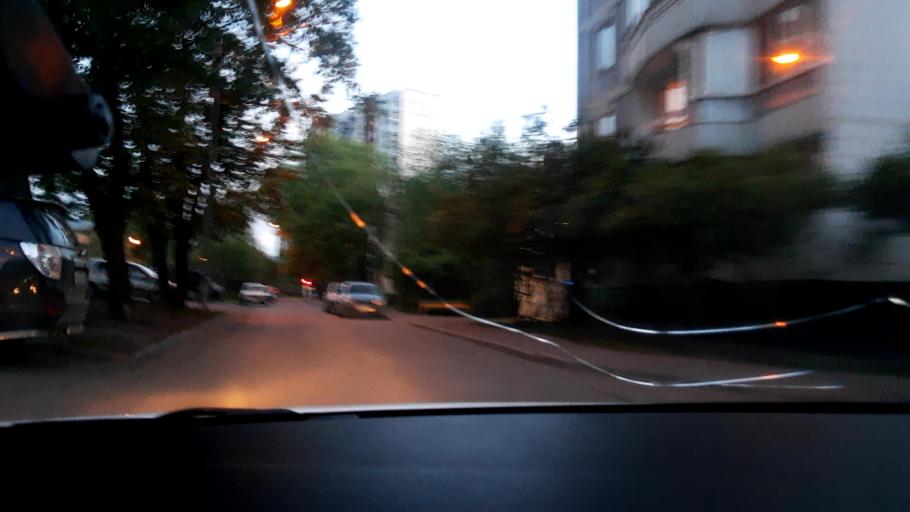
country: RU
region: Moscow
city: Businovo
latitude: 55.8760
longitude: 37.5125
